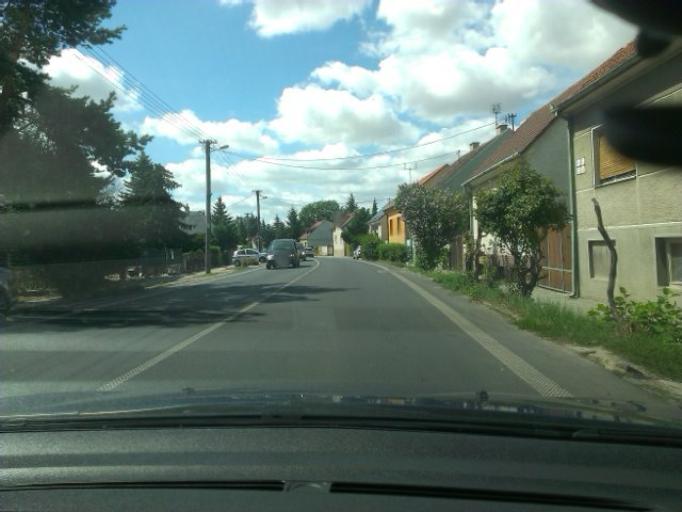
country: SK
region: Trnavsky
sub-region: Okres Trnava
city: Piestany
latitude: 48.6019
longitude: 17.8278
